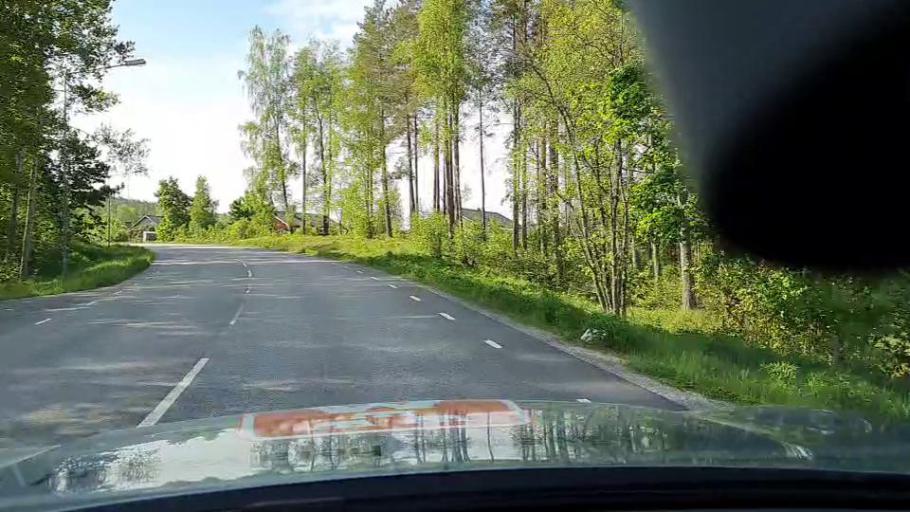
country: SE
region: Soedermanland
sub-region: Eskilstuna Kommun
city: Arla
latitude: 59.2901
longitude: 16.6756
